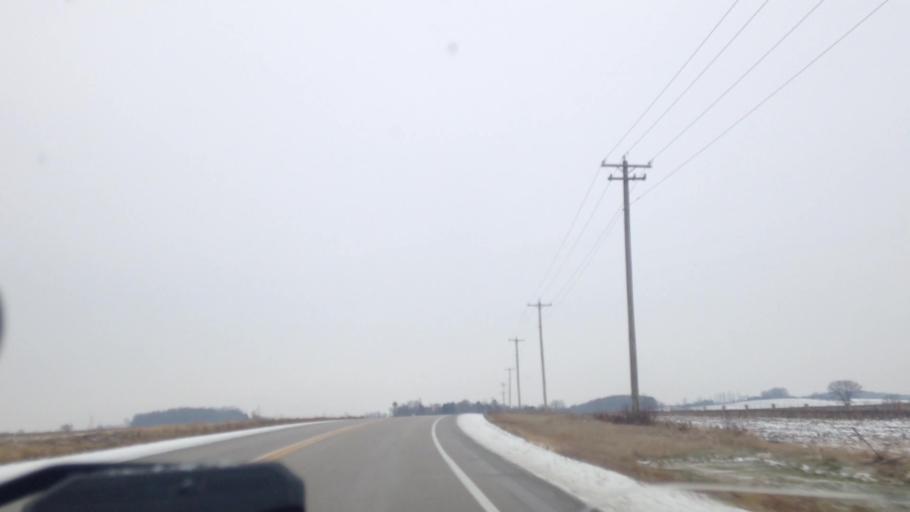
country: US
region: Wisconsin
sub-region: Dodge County
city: Hustisford
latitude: 43.3654
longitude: -88.5182
